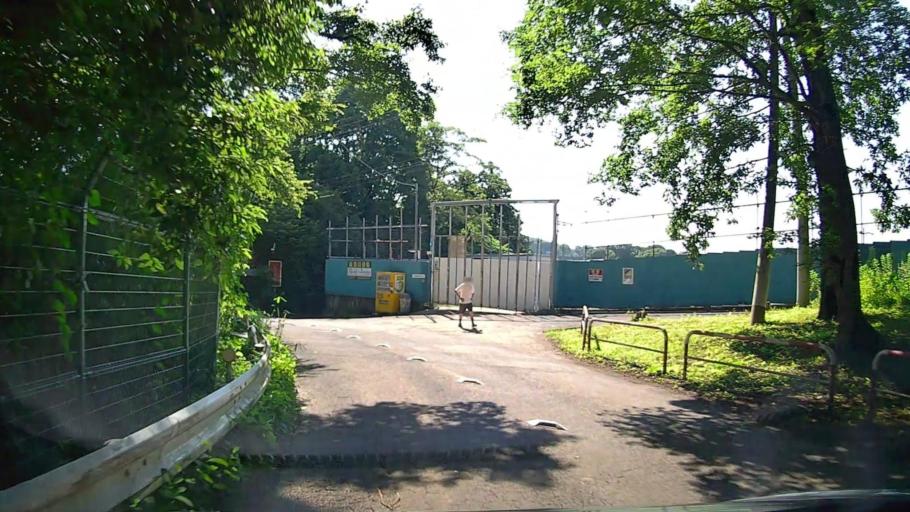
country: JP
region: Saitama
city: Tokorozawa
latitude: 35.7838
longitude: 139.4131
